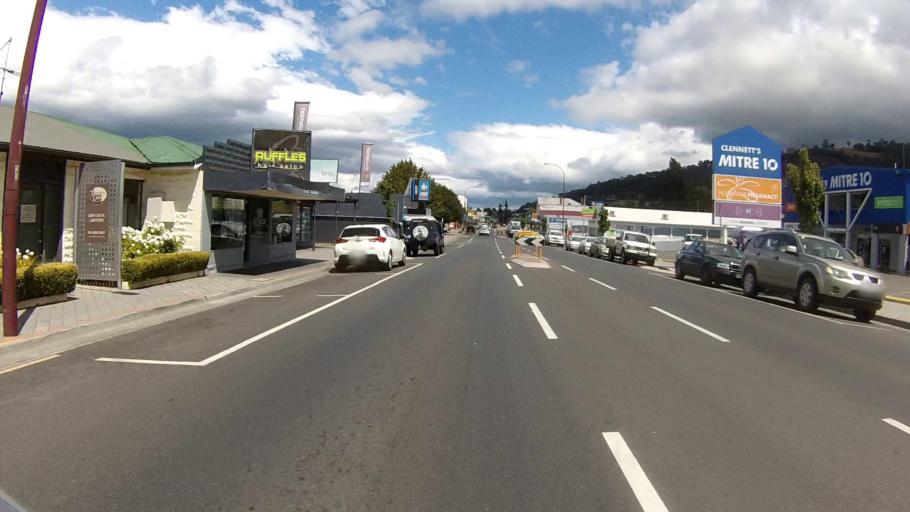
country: AU
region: Tasmania
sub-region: Huon Valley
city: Huonville
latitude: -43.0292
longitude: 147.0494
